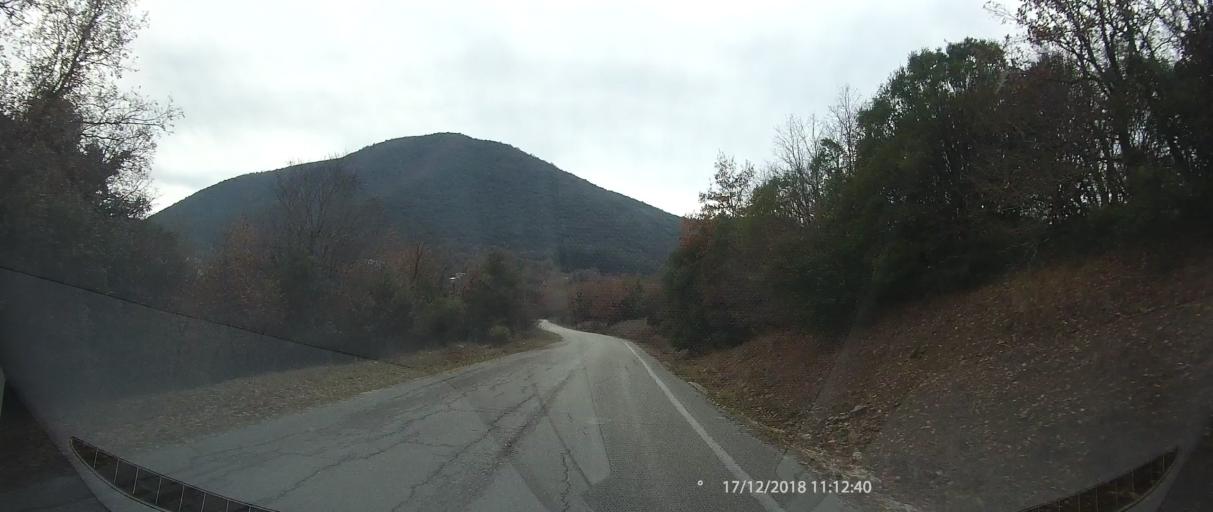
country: GR
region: Epirus
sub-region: Nomos Ioanninon
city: Kalpaki
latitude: 39.9402
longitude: 20.6739
